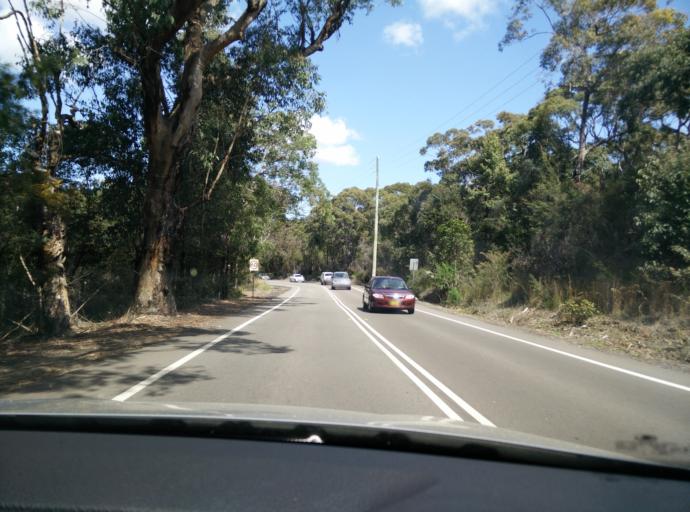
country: AU
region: New South Wales
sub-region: Gosford Shire
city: Blackwall
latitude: -33.4861
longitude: 151.3048
